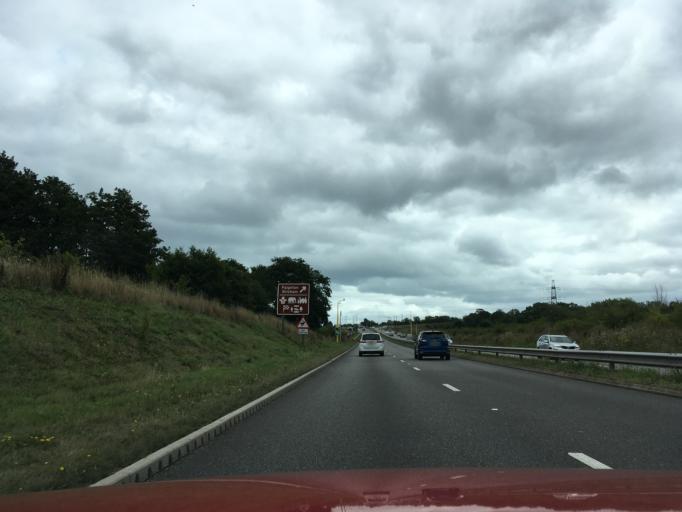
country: GB
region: England
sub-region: Devon
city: Kingskerswell
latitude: 50.4905
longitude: -3.5776
